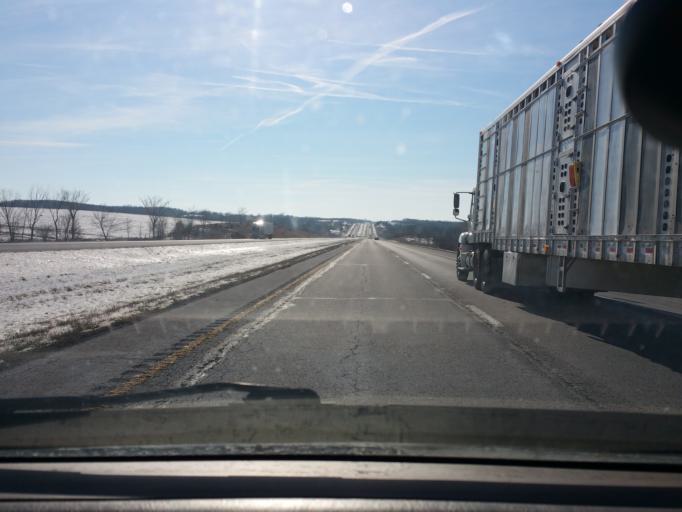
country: US
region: Missouri
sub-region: Harrison County
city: Bethany
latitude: 40.2425
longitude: -94.0130
